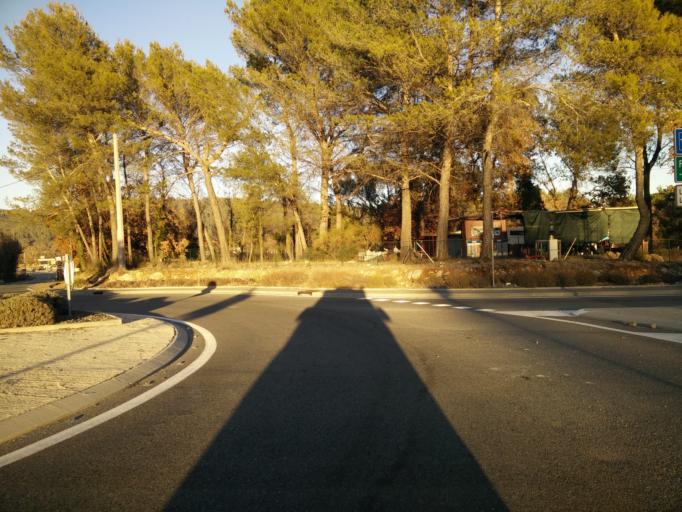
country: FR
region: Provence-Alpes-Cote d'Azur
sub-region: Departement du Var
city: Figanieres
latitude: 43.5532
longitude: 6.5239
